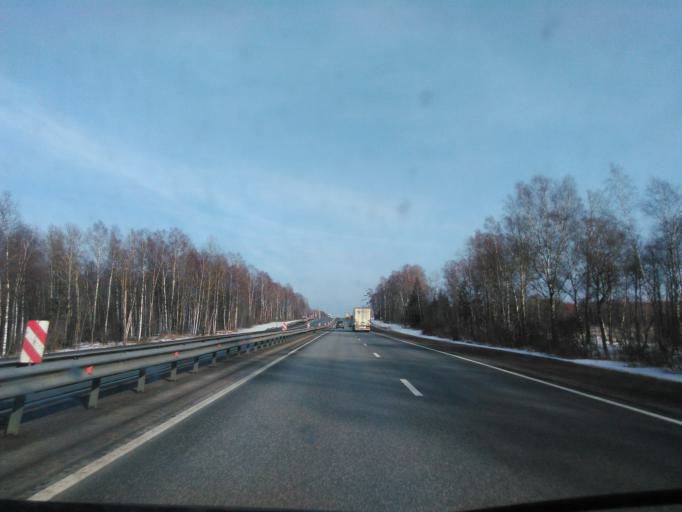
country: RU
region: Smolensk
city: Kholm-Zhirkovskiy
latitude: 55.1880
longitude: 33.7451
